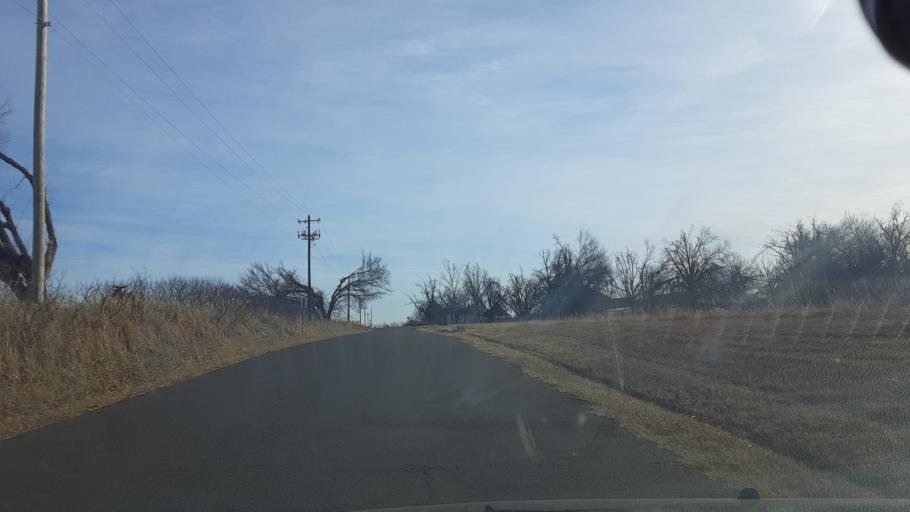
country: US
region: Oklahoma
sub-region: Logan County
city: Guthrie
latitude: 35.8924
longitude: -97.4126
